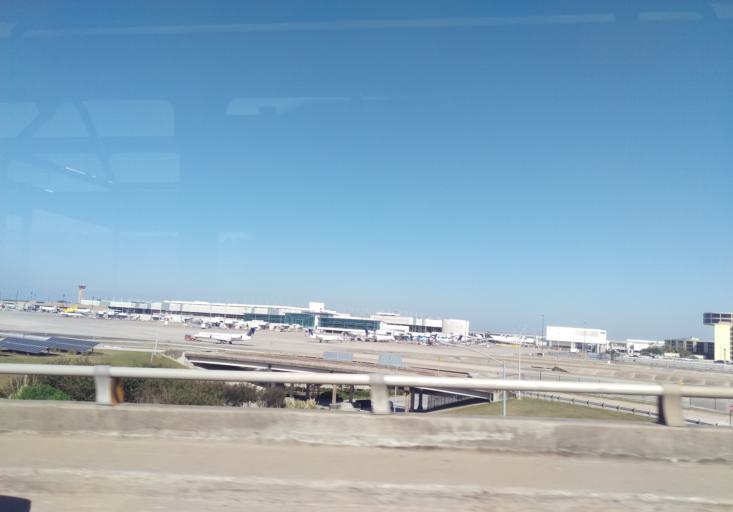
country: US
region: Texas
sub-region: Harris County
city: Aldine
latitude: 29.9816
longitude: -95.3422
